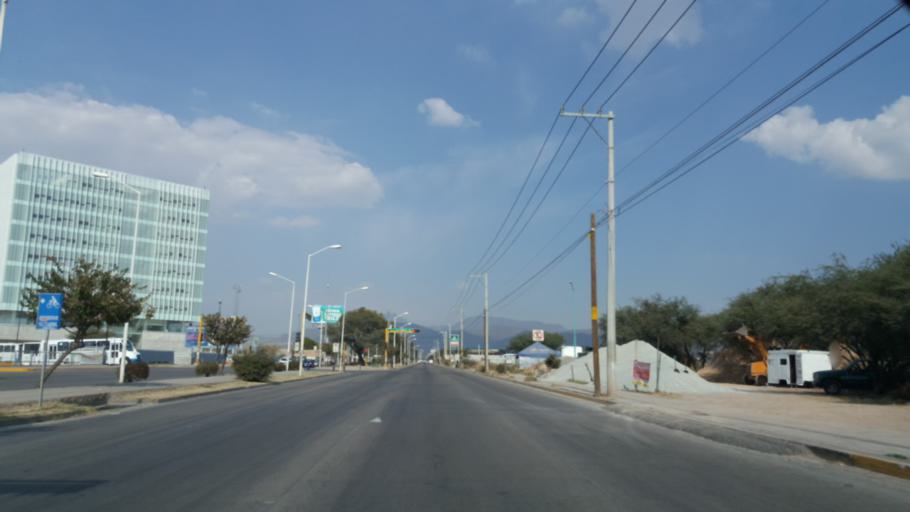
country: MX
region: Guanajuato
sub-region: Leon
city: Fraccionamiento Paraiso Real
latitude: 21.0939
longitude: -101.6172
